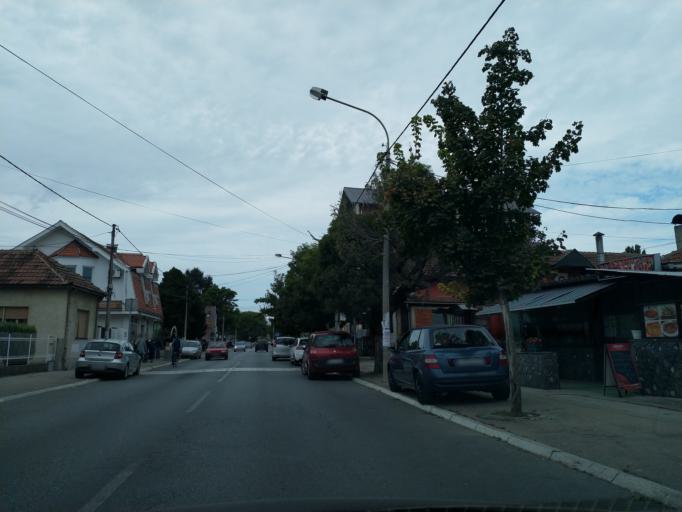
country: RS
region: Central Serbia
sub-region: Pomoravski Okrug
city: Jagodina
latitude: 43.9841
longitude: 21.2522
